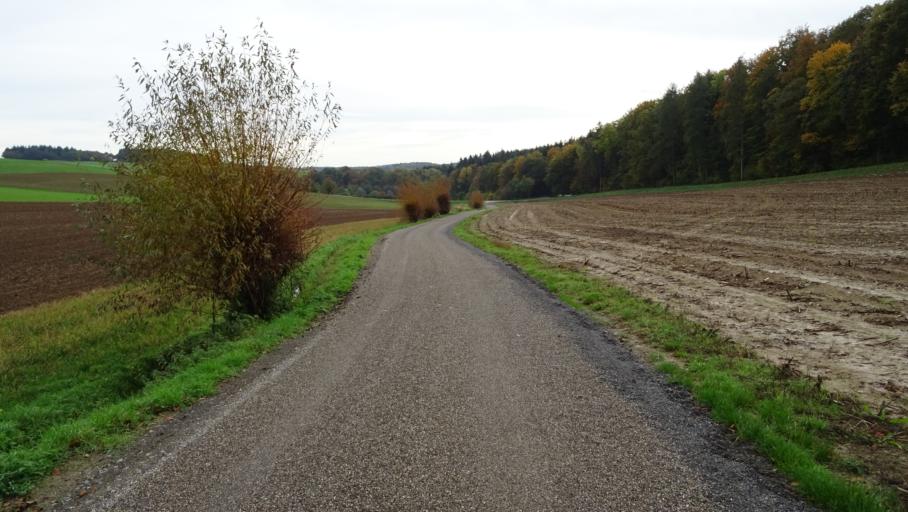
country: DE
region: Baden-Wuerttemberg
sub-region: Karlsruhe Region
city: Billigheim
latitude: 49.3418
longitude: 9.2178
